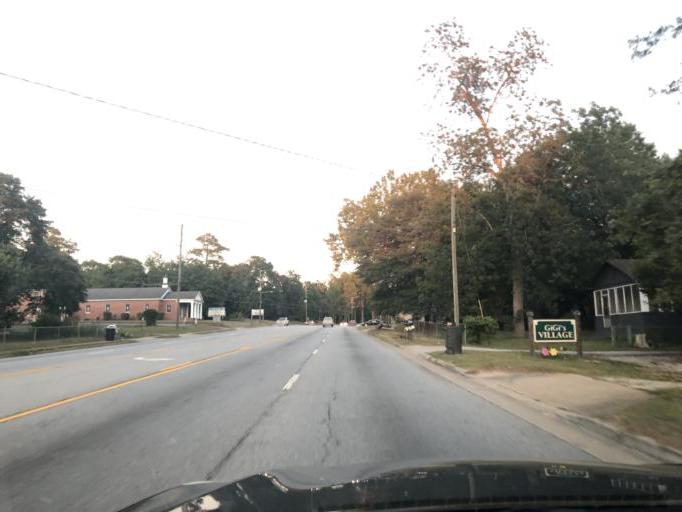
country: US
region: Georgia
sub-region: Muscogee County
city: Columbus
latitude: 32.4676
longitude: -84.9074
